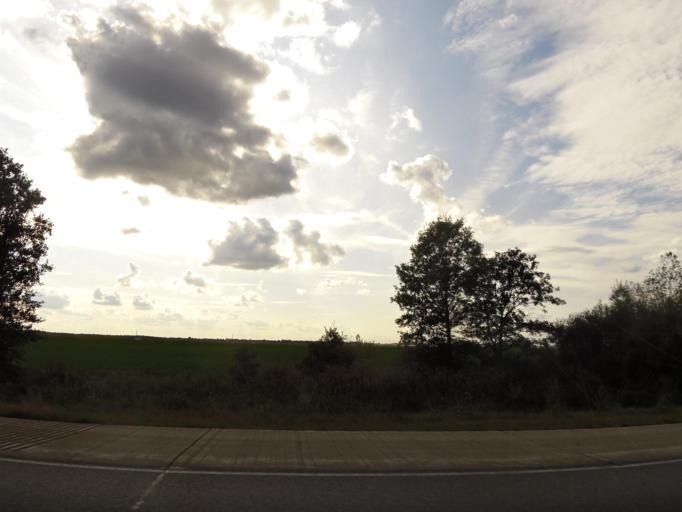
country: US
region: Indiana
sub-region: Newton County
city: Roselawn
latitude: 41.0373
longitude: -87.2713
